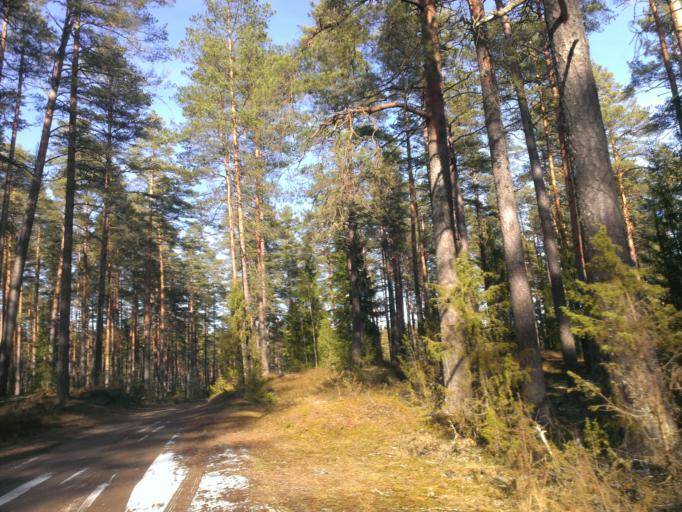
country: LV
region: Garkalne
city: Garkalne
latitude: 56.9619
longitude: 24.4556
